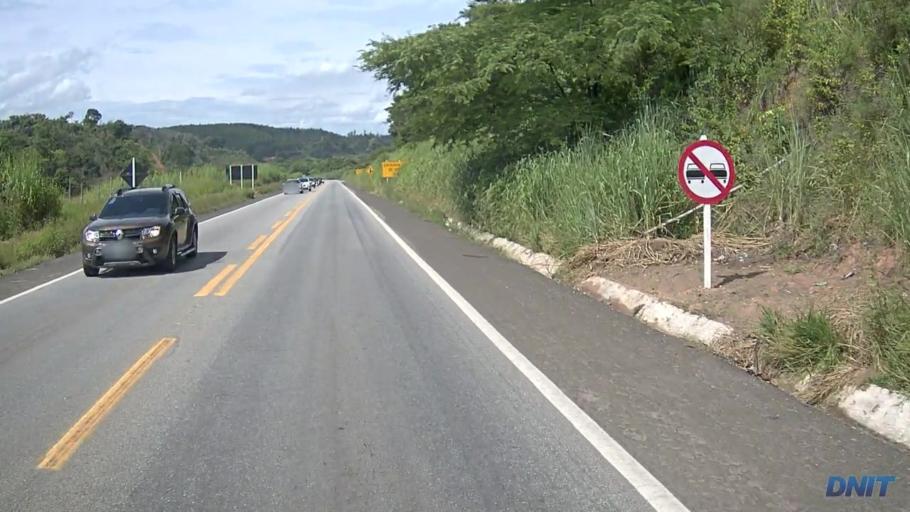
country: BR
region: Minas Gerais
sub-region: Ipaba
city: Ipaba
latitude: -19.3916
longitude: -42.4801
